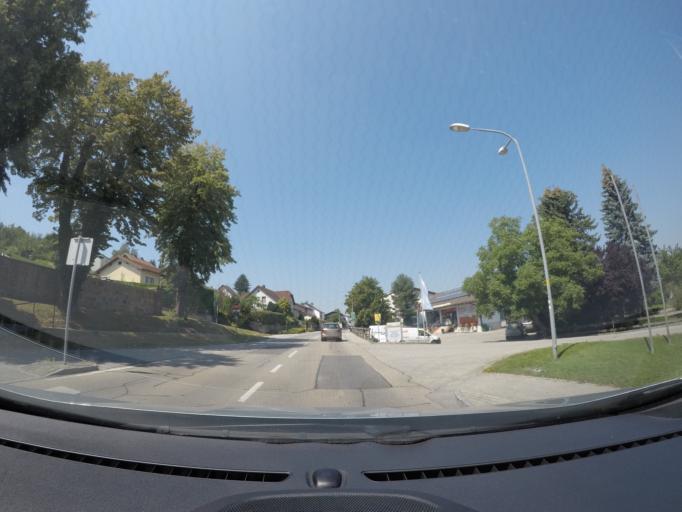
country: AT
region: Lower Austria
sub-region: Politischer Bezirk Sankt Polten
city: Maria-Anzbach
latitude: 48.1892
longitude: 15.9356
